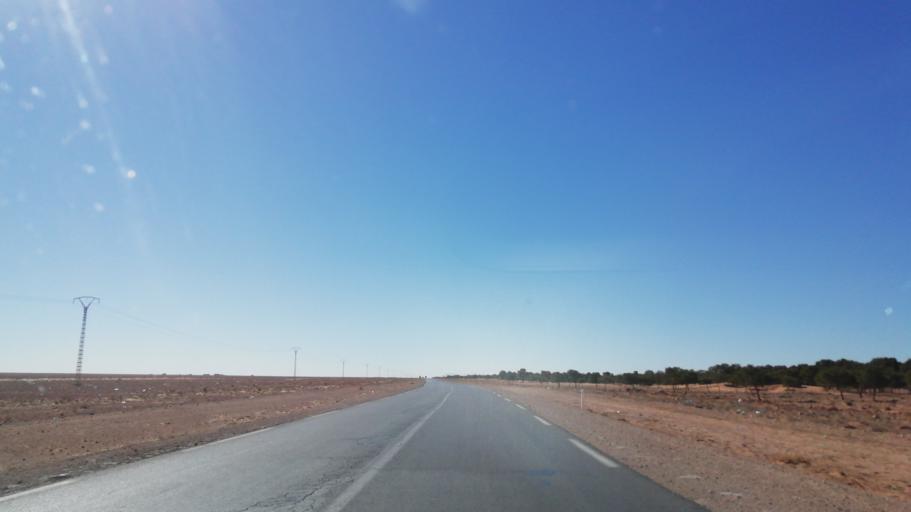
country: DZ
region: Saida
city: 'Ain el Hadjar
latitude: 34.0012
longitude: 0.0436
